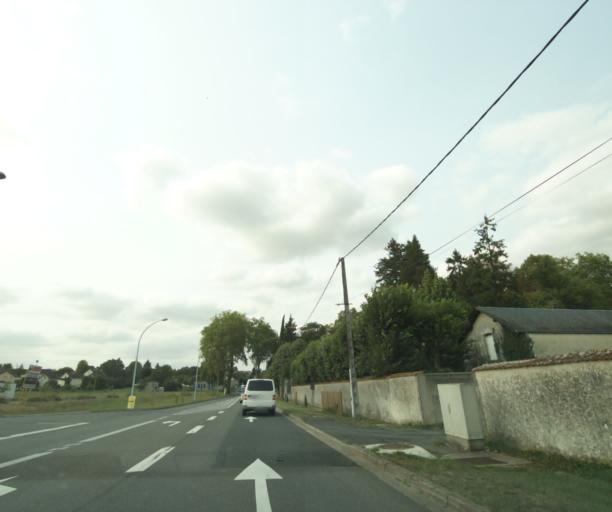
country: FR
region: Centre
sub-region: Departement de l'Indre
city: Chatillon-sur-Indre
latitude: 46.9785
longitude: 1.1794
